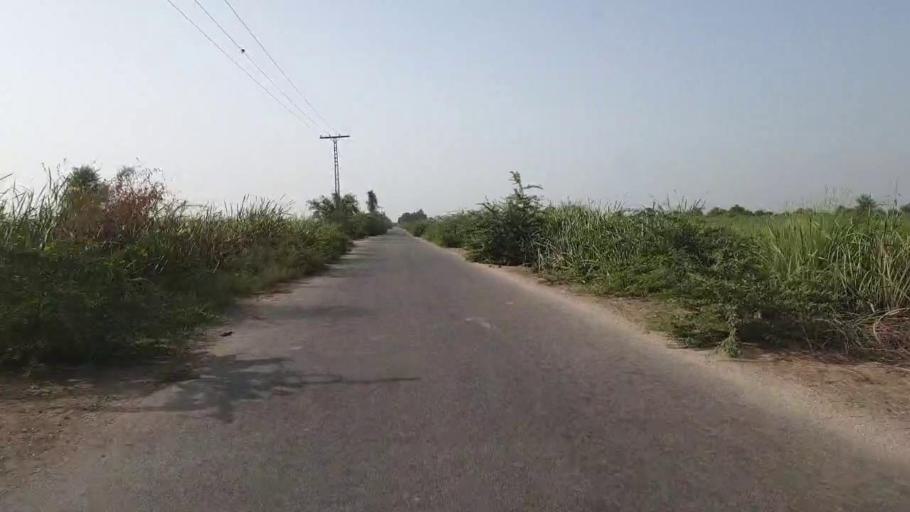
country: PK
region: Sindh
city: Jam Sahib
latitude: 26.4014
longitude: 68.8779
